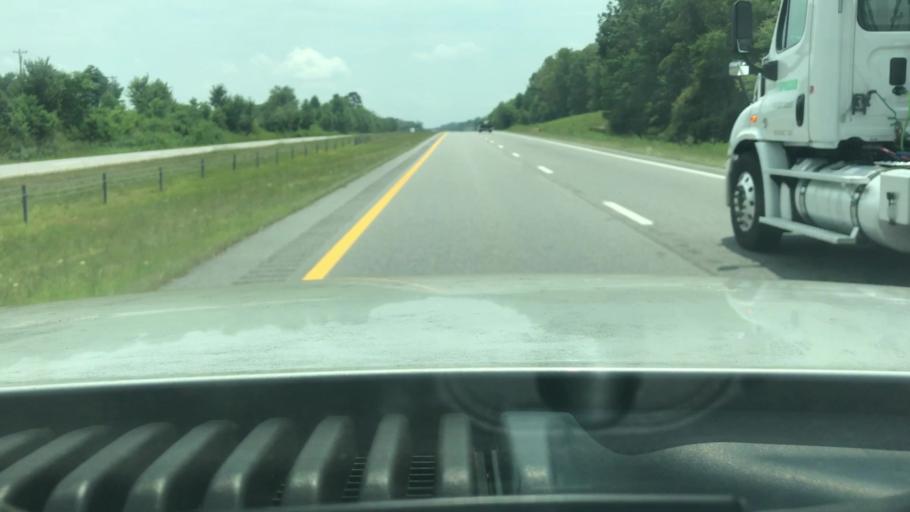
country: US
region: North Carolina
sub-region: Yadkin County
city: Jonesville
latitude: 36.1368
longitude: -80.8603
